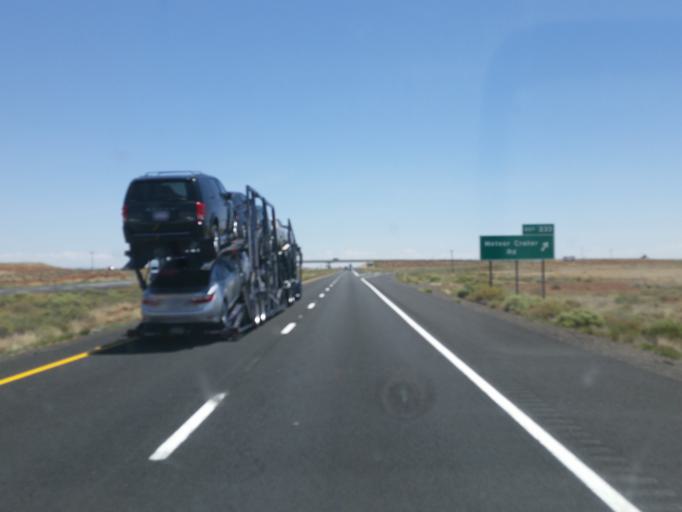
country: US
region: Arizona
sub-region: Coconino County
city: LeChee
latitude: 35.1108
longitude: -111.0376
